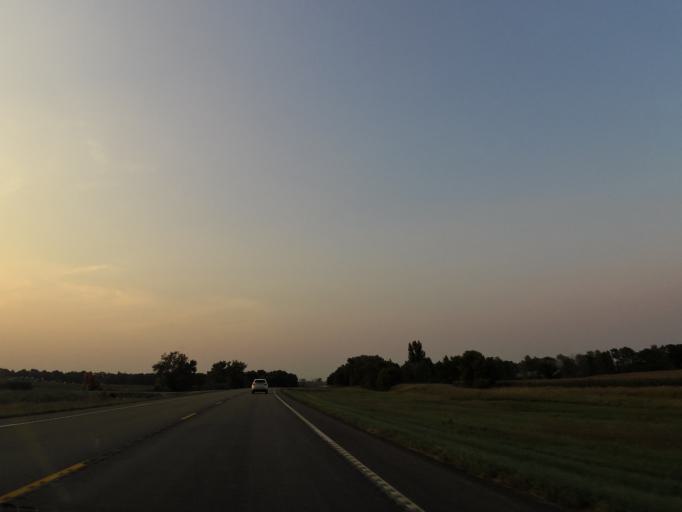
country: US
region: North Dakota
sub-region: Walsh County
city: Park River
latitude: 48.1758
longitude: -97.6232
